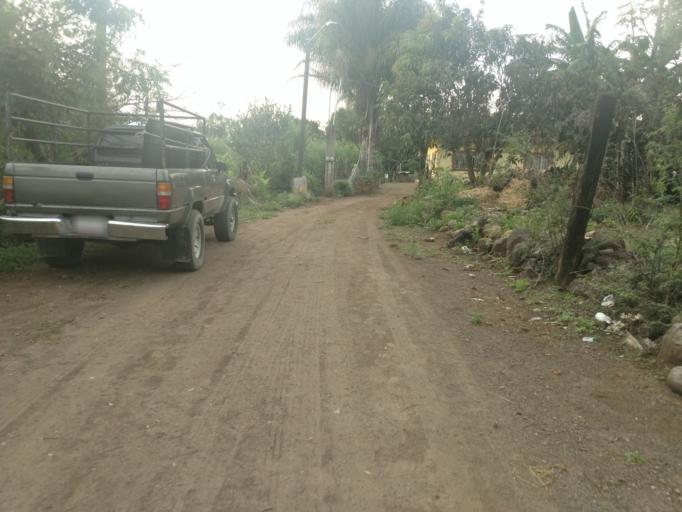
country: MX
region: Nayarit
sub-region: Tepic
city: La Corregidora
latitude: 21.4634
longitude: -104.8042
